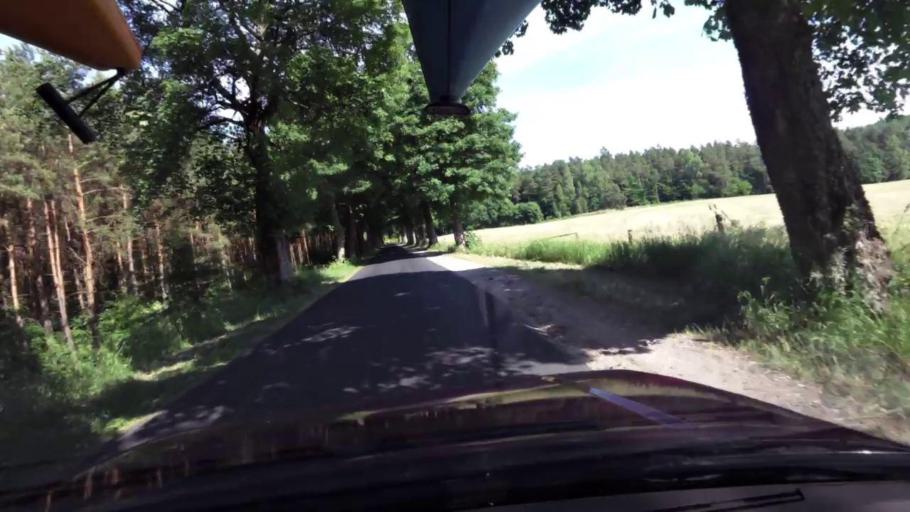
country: PL
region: Pomeranian Voivodeship
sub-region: Powiat slupski
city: Kepice
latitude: 54.1292
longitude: 16.9333
